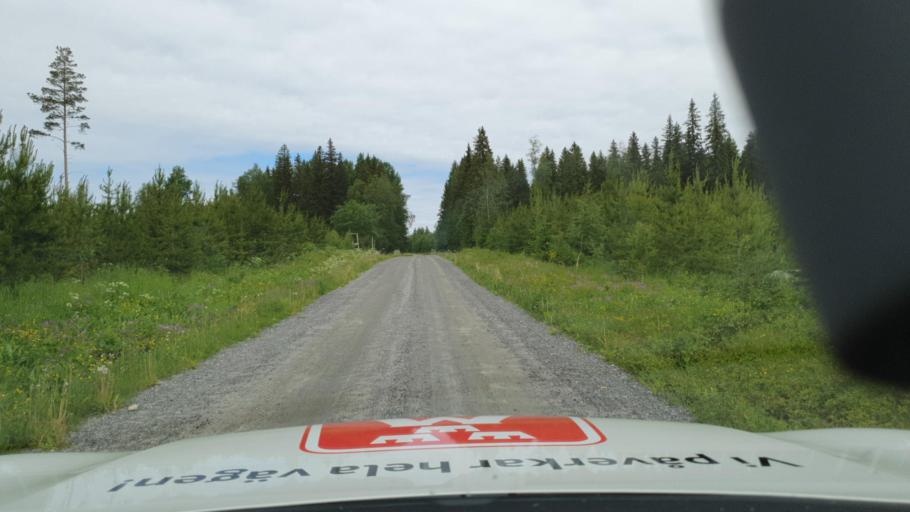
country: SE
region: Vaesterbotten
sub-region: Skelleftea Kommun
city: Langsele
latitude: 64.4733
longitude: 20.2640
